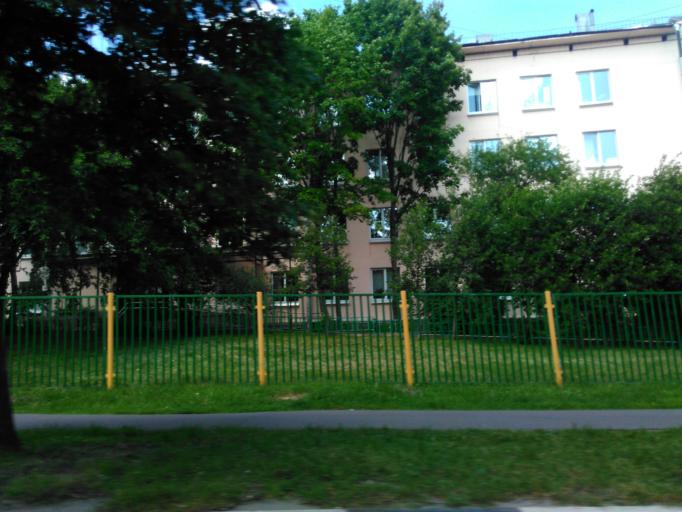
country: RU
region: Moskovskaya
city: Cheremushki
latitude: 55.6673
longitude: 37.5655
